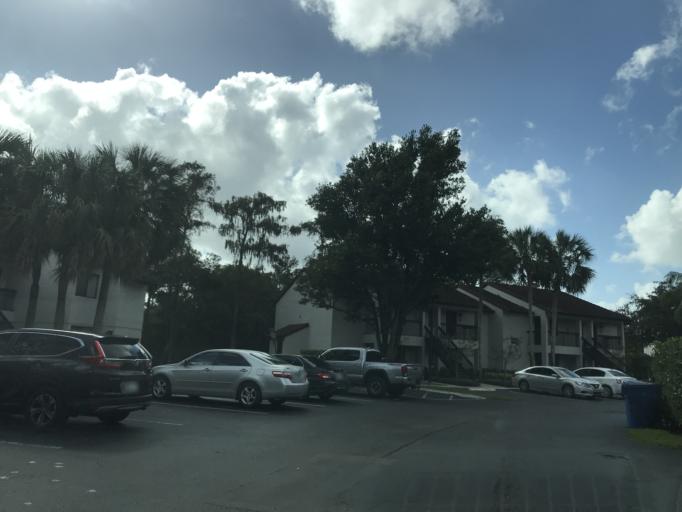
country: US
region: Florida
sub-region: Broward County
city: Coconut Creek
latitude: 26.2718
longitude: -80.1910
